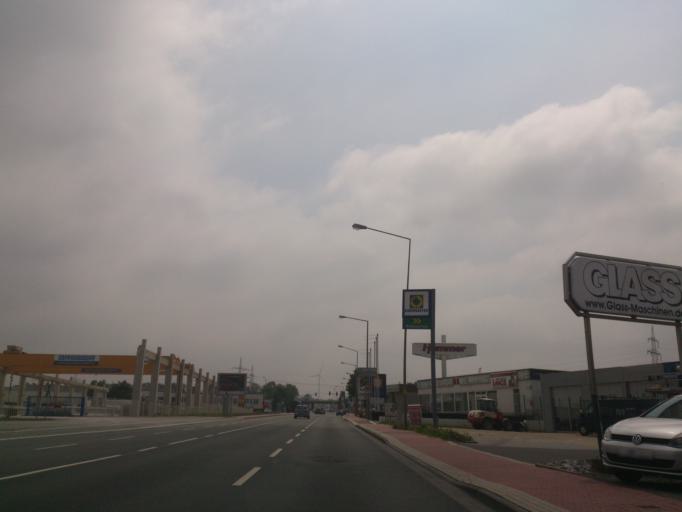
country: DE
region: North Rhine-Westphalia
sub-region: Regierungsbezirk Detmold
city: Paderborn
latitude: 51.7051
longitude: 8.7242
